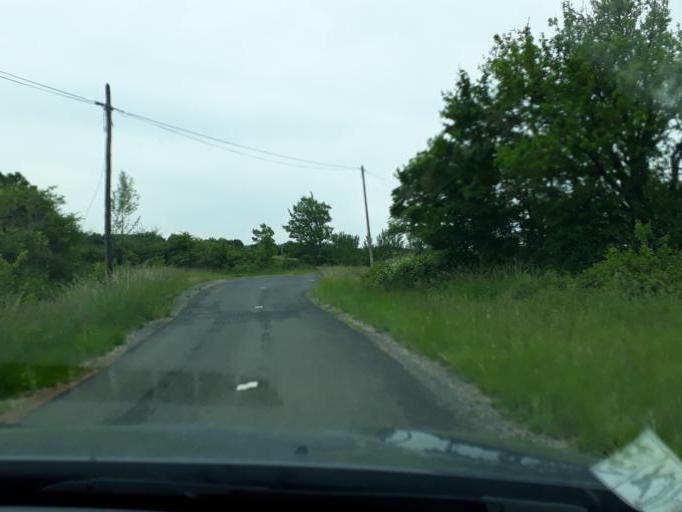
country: FR
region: Languedoc-Roussillon
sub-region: Departement de l'Herault
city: Lodeve
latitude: 43.8312
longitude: 3.2737
